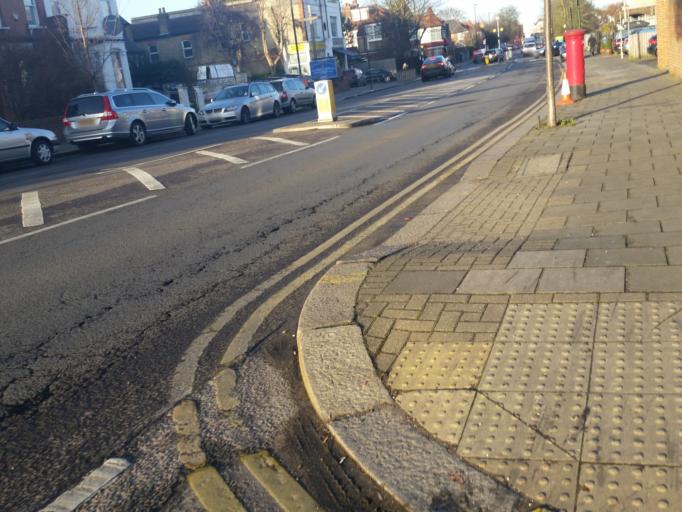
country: GB
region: England
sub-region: Greater London
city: Enfield
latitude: 51.6260
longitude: -0.0991
